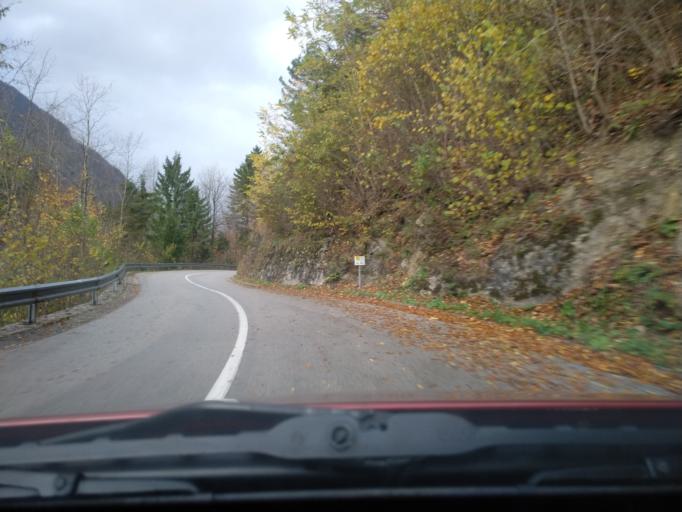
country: SI
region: Kamnik
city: Mekinje
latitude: 46.2996
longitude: 14.6108
